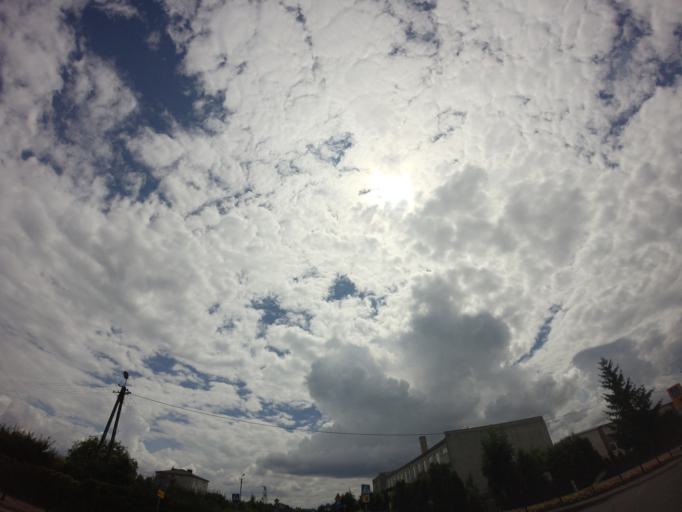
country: PL
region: Lublin Voivodeship
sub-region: Powiat opolski
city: Laziska
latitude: 51.1422
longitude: 21.8795
